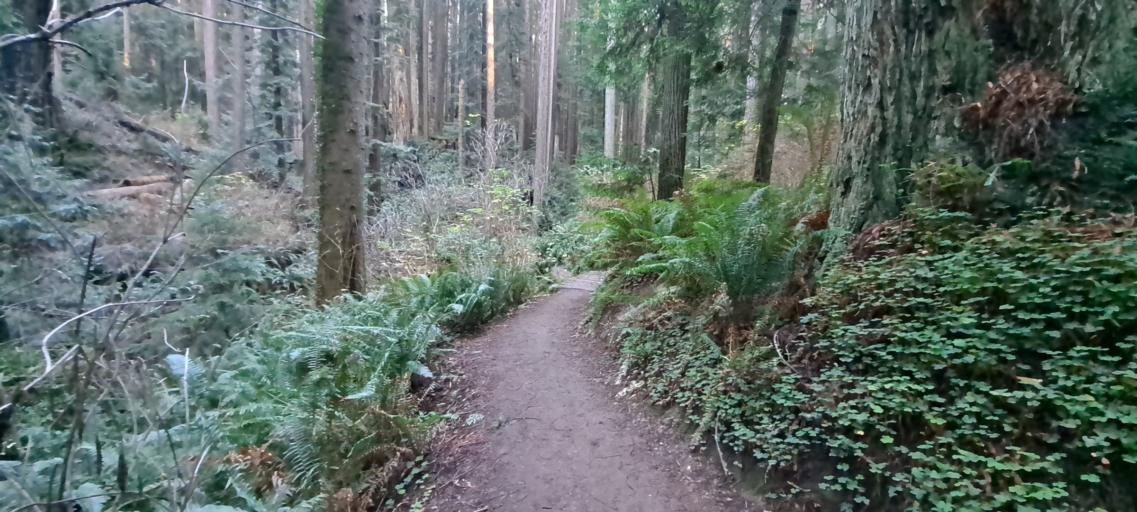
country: US
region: California
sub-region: Humboldt County
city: Arcata
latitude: 40.8705
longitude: -124.0704
